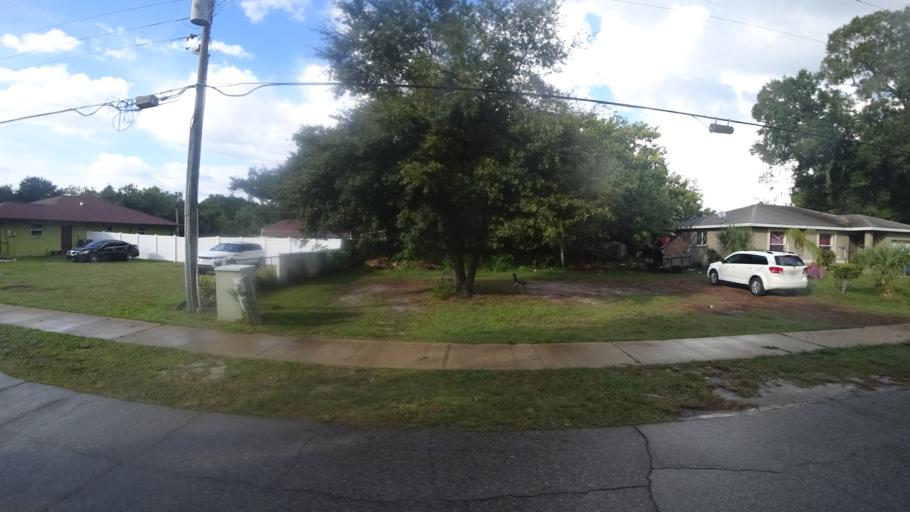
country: US
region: Florida
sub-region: Manatee County
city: Memphis
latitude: 27.5321
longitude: -82.5580
